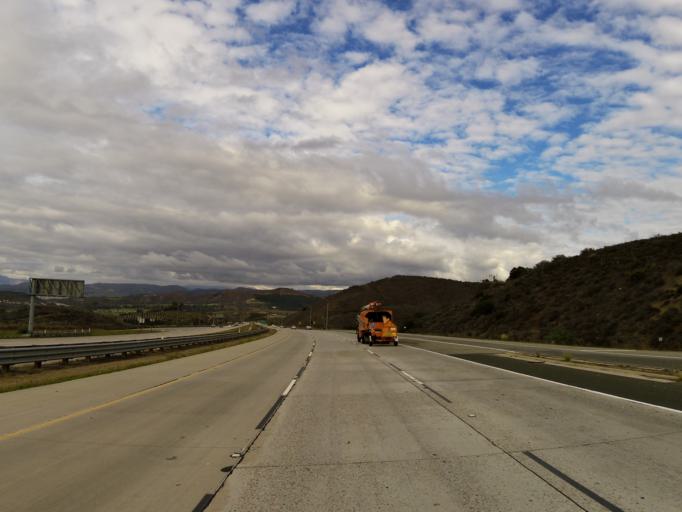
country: US
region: California
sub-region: Ventura County
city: Moorpark
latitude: 34.2424
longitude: -118.8396
